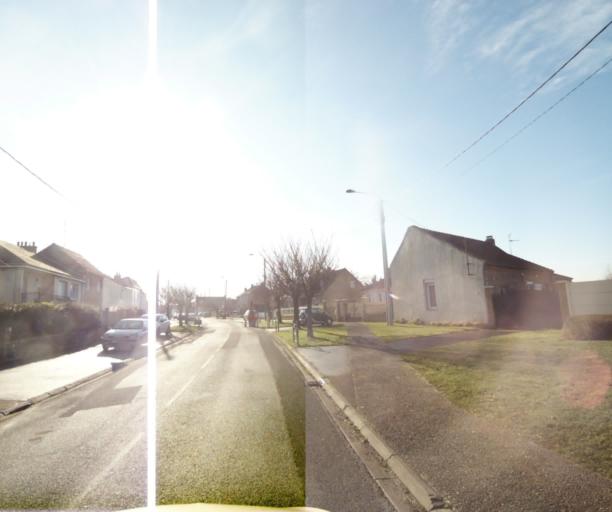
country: FR
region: Nord-Pas-de-Calais
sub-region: Departement du Nord
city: Trith-Saint-Leger
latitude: 50.3148
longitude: 3.4843
